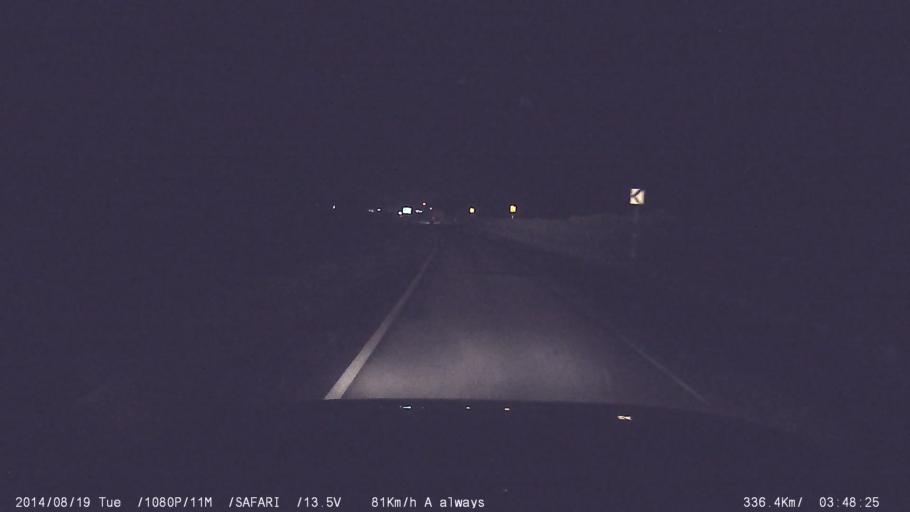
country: IN
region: Tamil Nadu
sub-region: Erode
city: Vijayapuri
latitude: 11.2376
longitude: 77.5074
